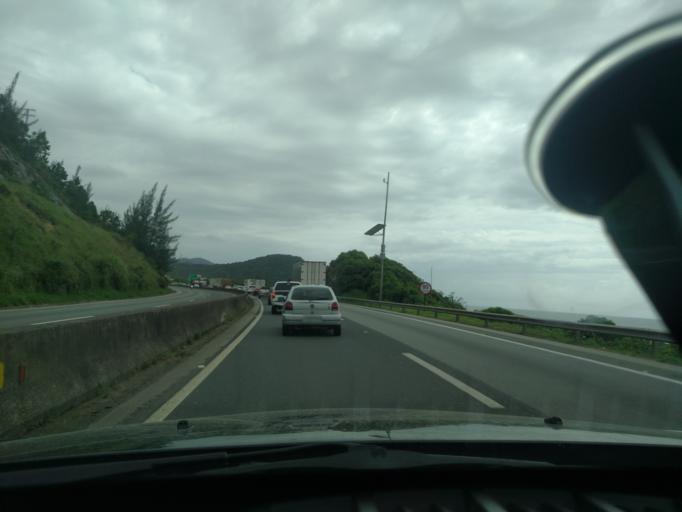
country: BR
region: Santa Catarina
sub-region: Itapema
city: Itapema
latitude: -27.0714
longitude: -48.5958
